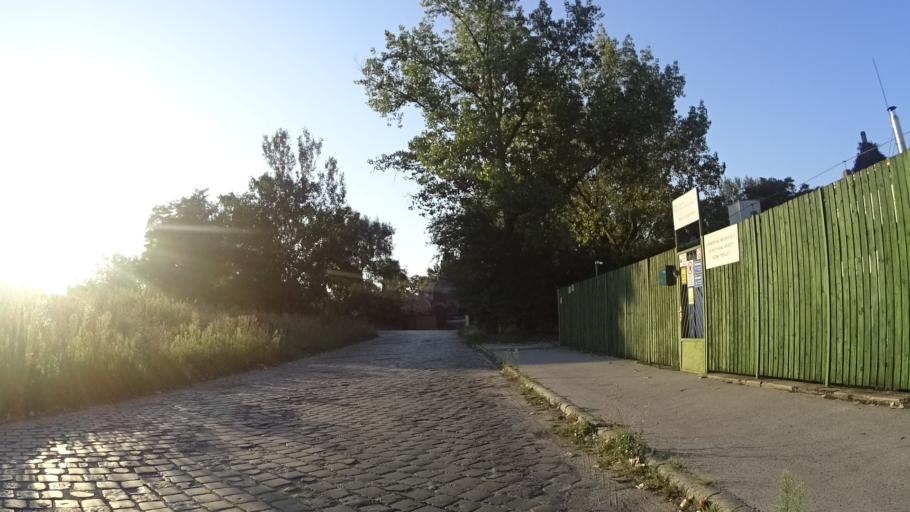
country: HU
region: Budapest
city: Budapest XXII. keruelet
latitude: 47.4072
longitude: 19.0317
